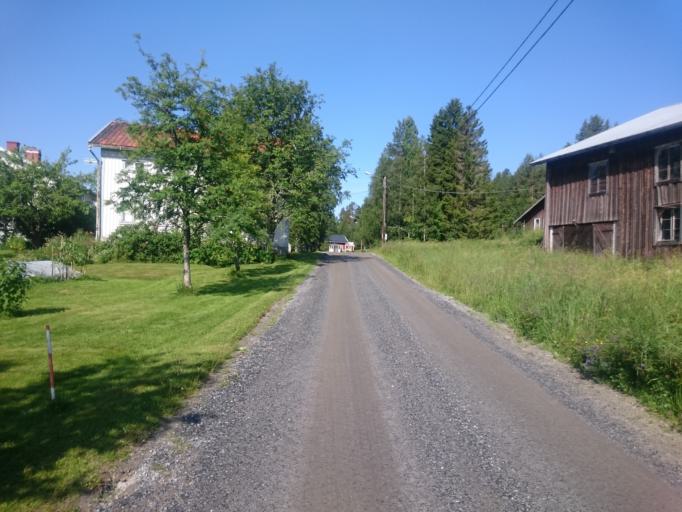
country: SE
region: Vaesternorrland
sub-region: OErnskoeldsviks Kommun
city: Bredbyn
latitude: 63.3011
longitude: 18.2611
